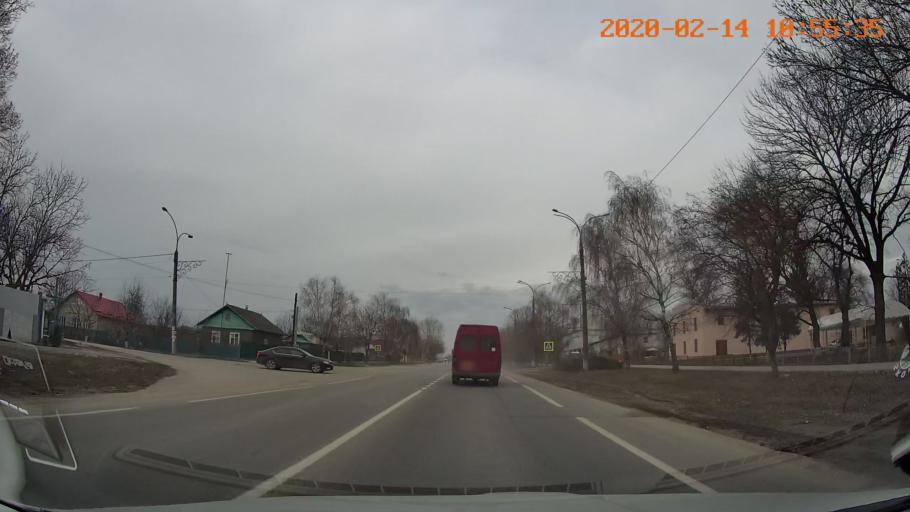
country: MD
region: Raionul Edinet
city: Edinet
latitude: 48.1158
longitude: 27.3905
